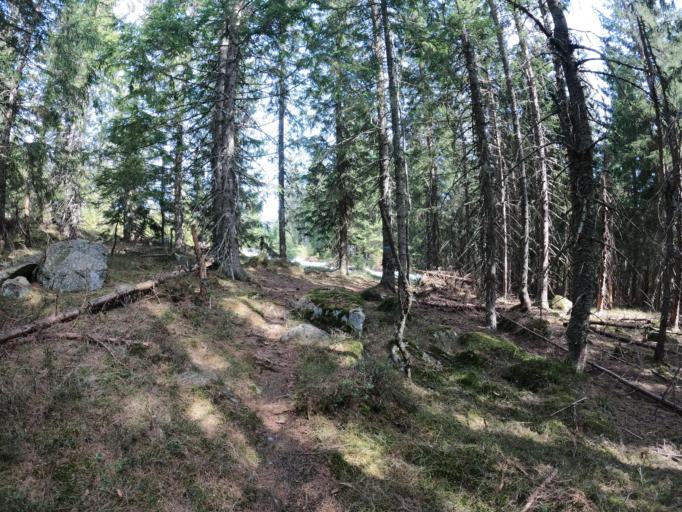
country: NO
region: Akershus
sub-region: Nittedal
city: Aneby
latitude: 60.2421
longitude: 10.8661
